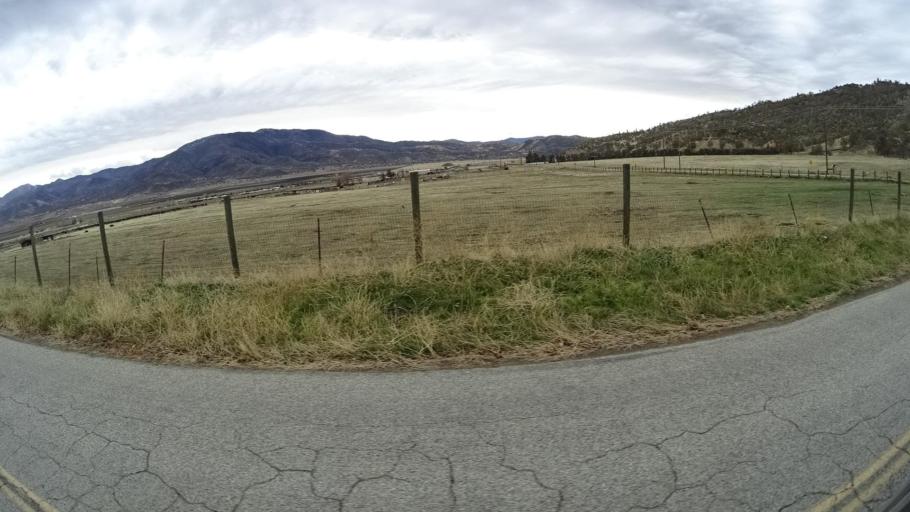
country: US
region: California
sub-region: Kern County
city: Bear Valley Springs
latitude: 35.1243
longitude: -118.6266
